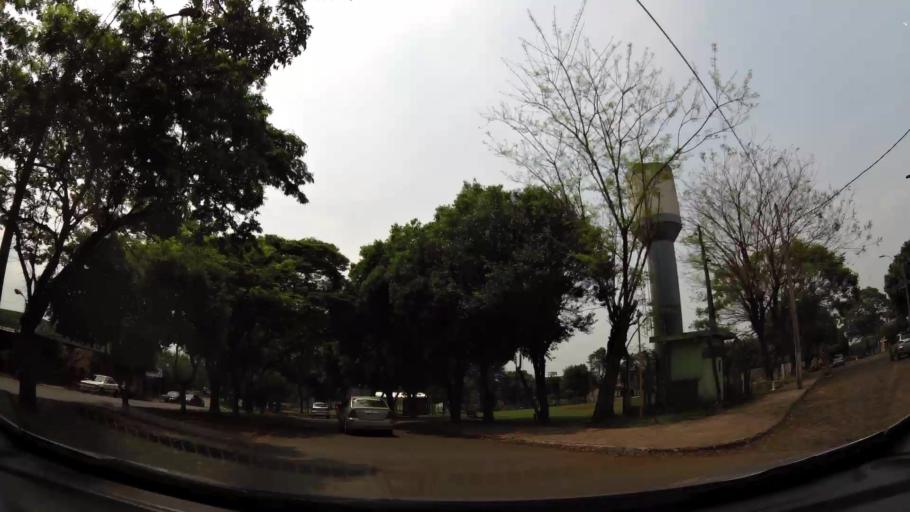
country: PY
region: Alto Parana
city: Presidente Franco
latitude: -25.5559
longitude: -54.6172
